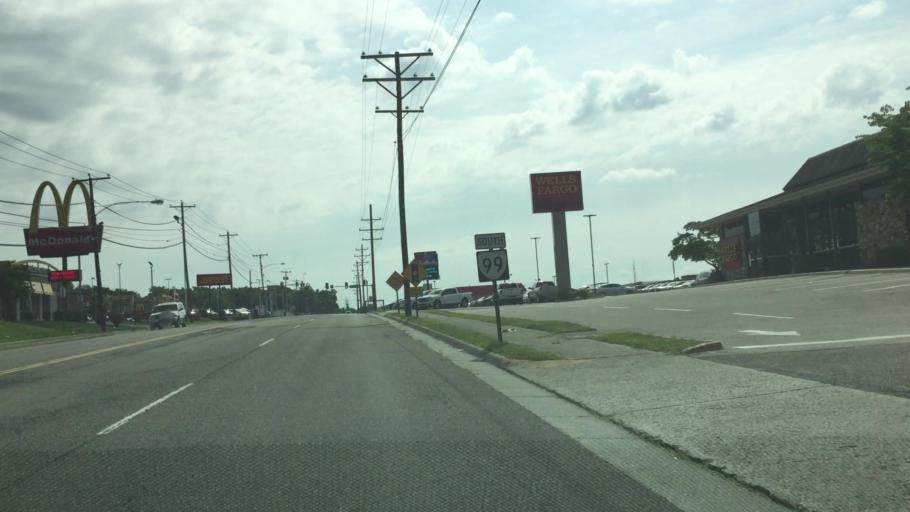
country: US
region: Virginia
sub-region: Pulaski County
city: Pulaski
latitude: 37.0485
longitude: -80.7638
